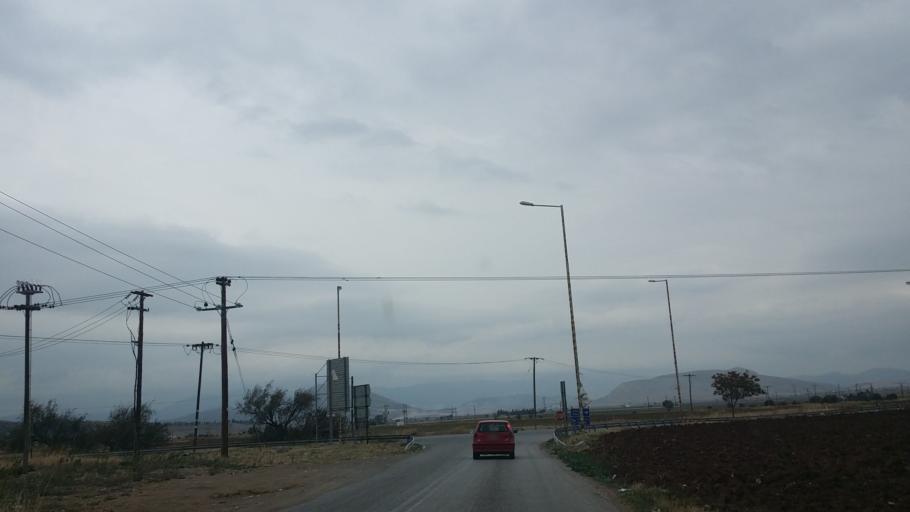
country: GR
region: Central Greece
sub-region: Nomos Voiotias
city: Thivai
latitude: 38.3265
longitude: 23.2732
